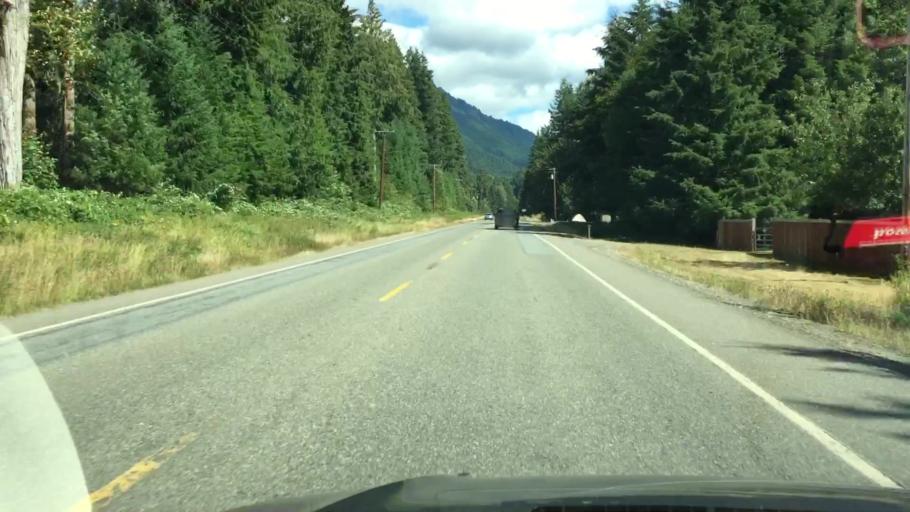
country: US
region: Washington
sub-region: Pierce County
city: Eatonville
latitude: 46.7572
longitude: -121.9920
